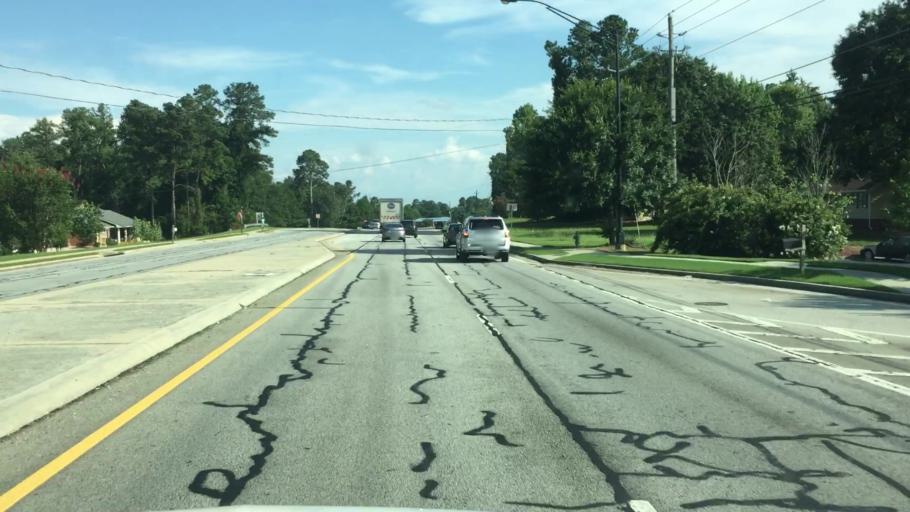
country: US
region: Georgia
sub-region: Gwinnett County
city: Snellville
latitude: 33.8319
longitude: -84.0317
